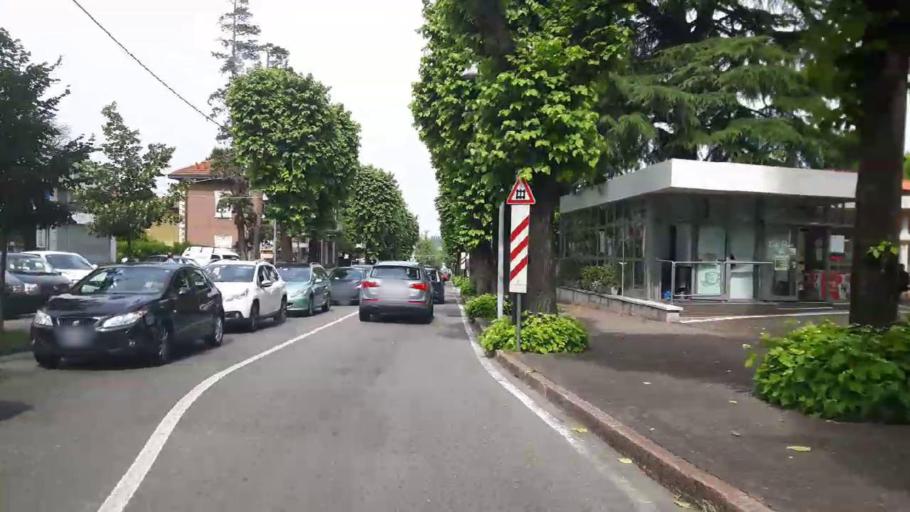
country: IT
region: Lombardy
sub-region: Provincia di Como
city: Fino Mornasco
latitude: 45.7463
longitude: 9.0494
